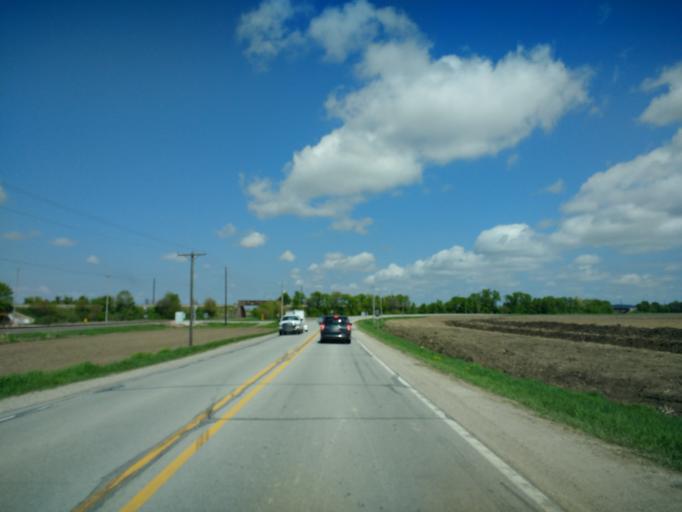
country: US
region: Iowa
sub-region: Harrison County
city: Missouri Valley
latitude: 41.4980
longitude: -95.8929
